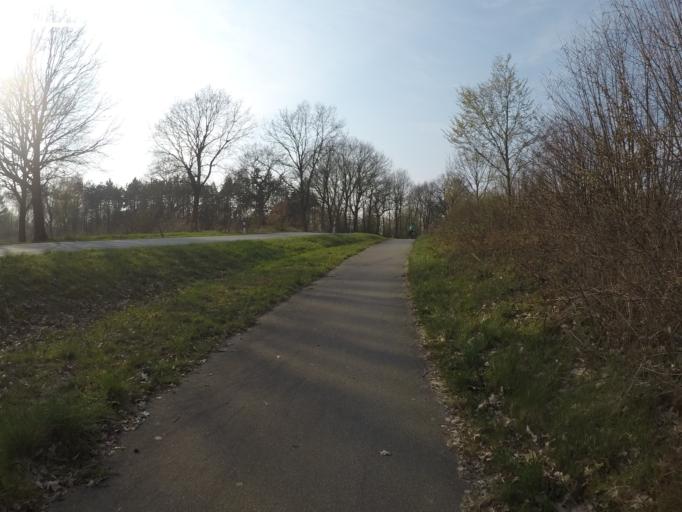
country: DE
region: Schleswig-Holstein
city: Kukels
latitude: 53.9130
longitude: 10.2242
